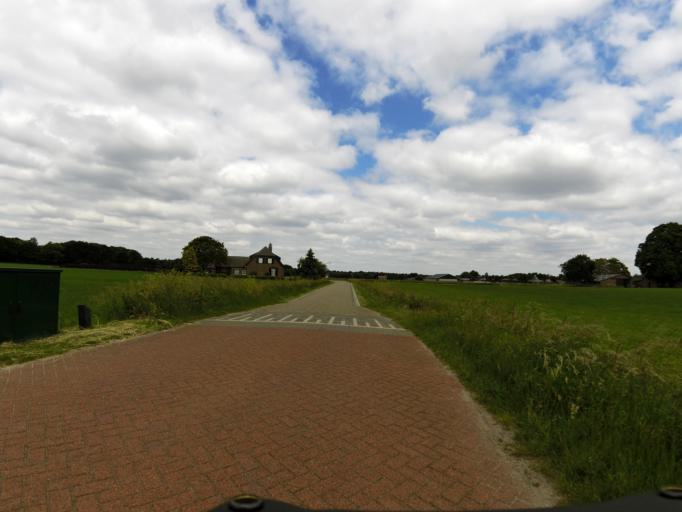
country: NL
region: North Brabant
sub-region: Gemeente Baarle-Nassau
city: Baarle-Nassau
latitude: 51.4800
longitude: 4.9408
